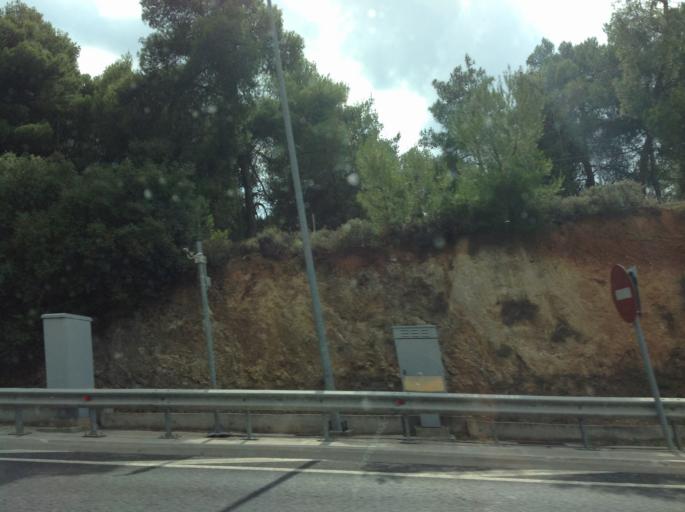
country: GR
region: Attica
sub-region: Nomarchia Athinas
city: Agia Paraskevi
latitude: 38.0063
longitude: 23.8367
